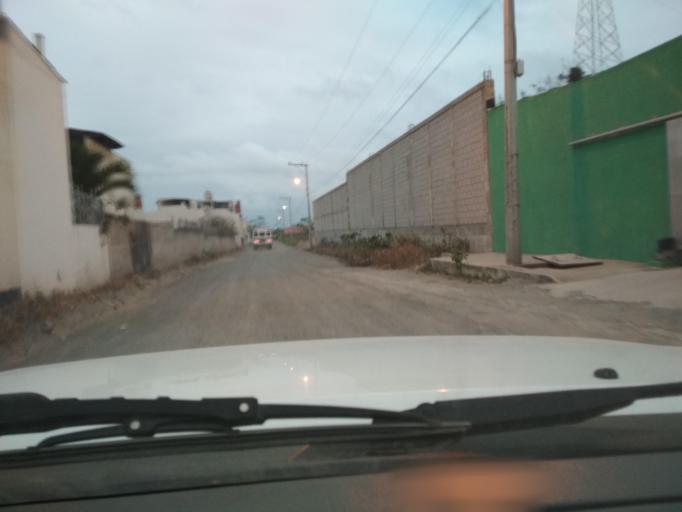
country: MX
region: Veracruz
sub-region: Medellin
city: Fraccionamiento Arboledas San Ramon
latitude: 19.0870
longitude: -96.1299
